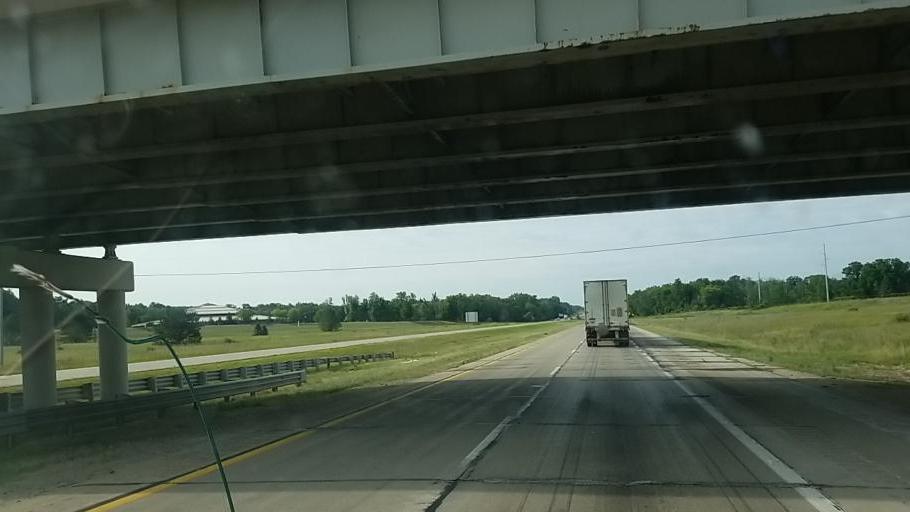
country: US
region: Michigan
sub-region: Eaton County
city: Charlotte
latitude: 42.5533
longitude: -84.8212
